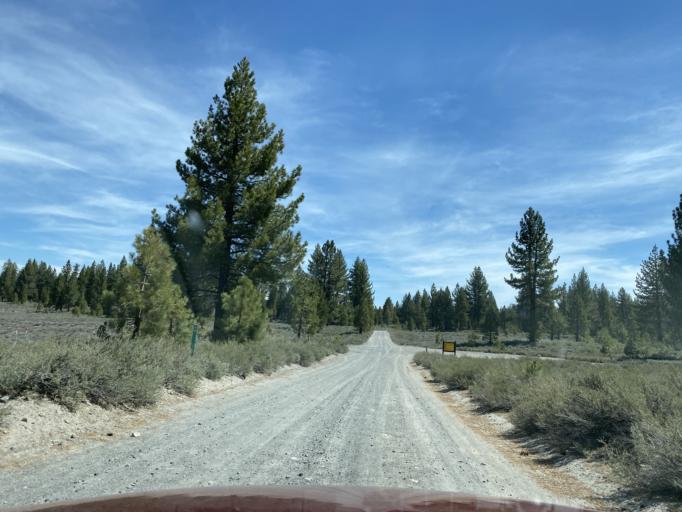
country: US
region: California
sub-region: Mono County
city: Mammoth Lakes
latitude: 37.7706
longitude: -119.0185
